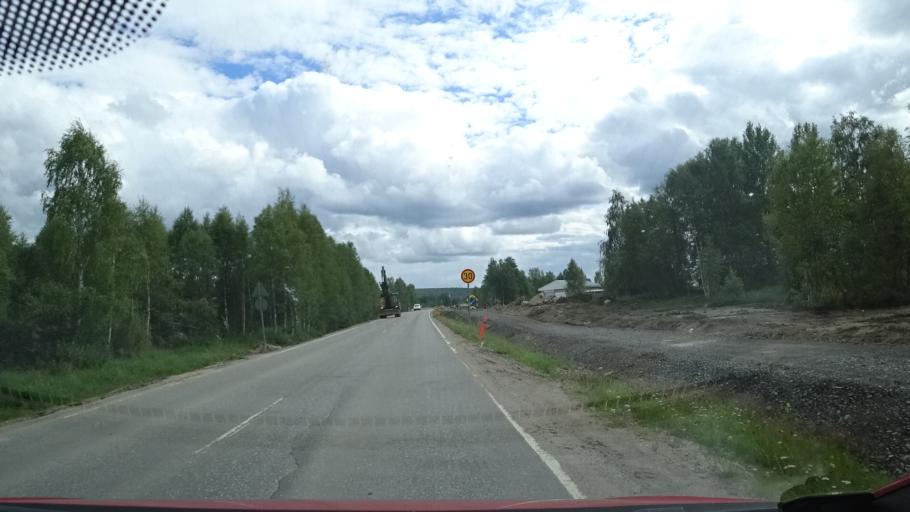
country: FI
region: Lapland
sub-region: Rovaniemi
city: Rovaniemi
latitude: 66.5288
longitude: 25.7396
